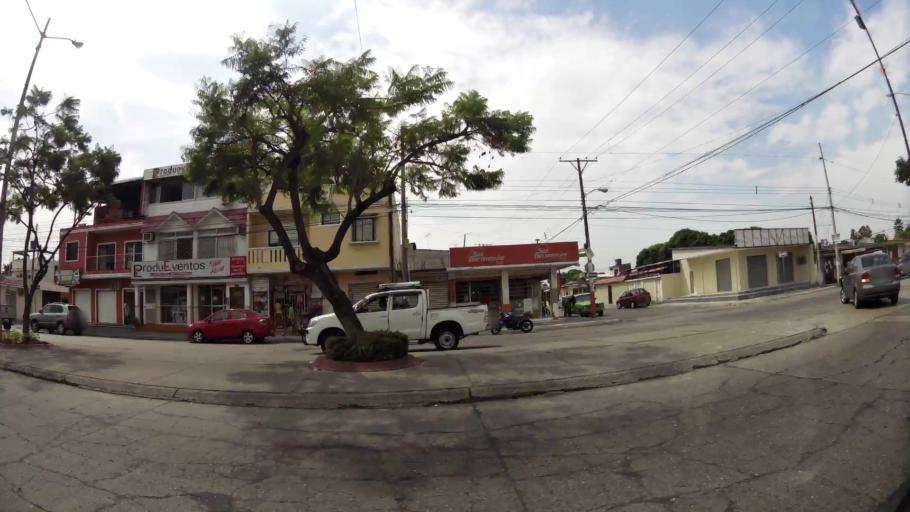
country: EC
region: Guayas
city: Eloy Alfaro
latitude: -2.1214
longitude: -79.8983
